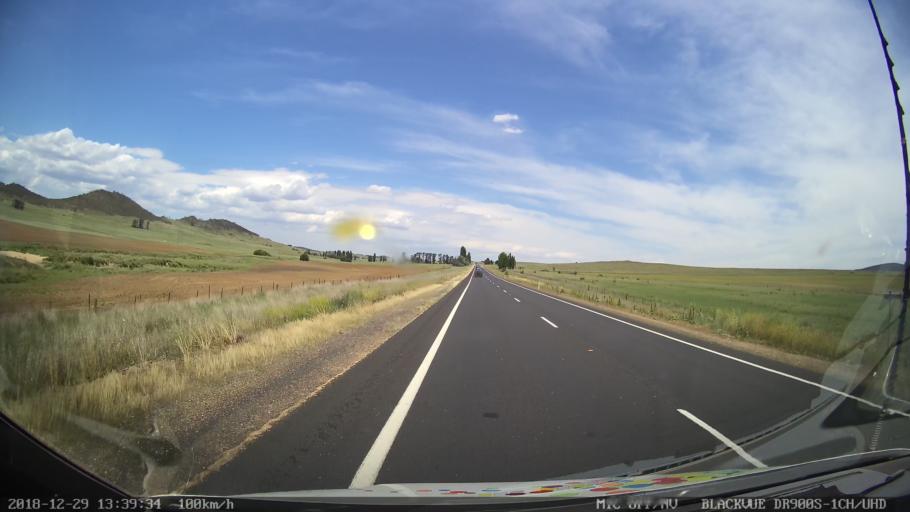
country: AU
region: New South Wales
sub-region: Cooma-Monaro
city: Cooma
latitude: -36.0150
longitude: 149.1477
